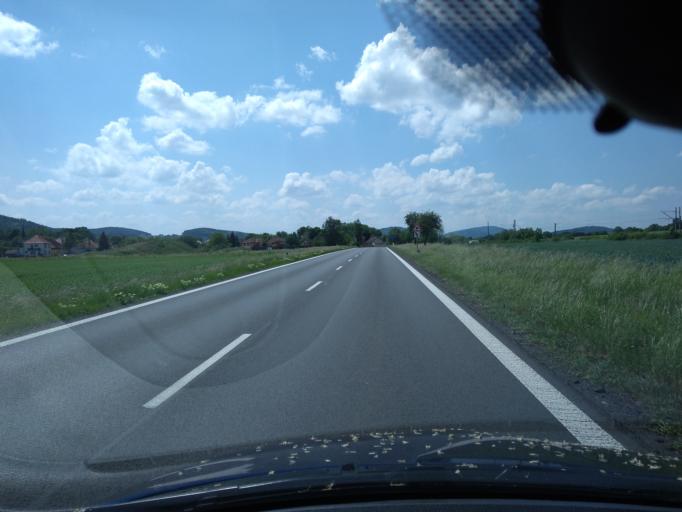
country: CZ
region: Plzensky
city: Prestice
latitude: 49.5521
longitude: 13.3163
